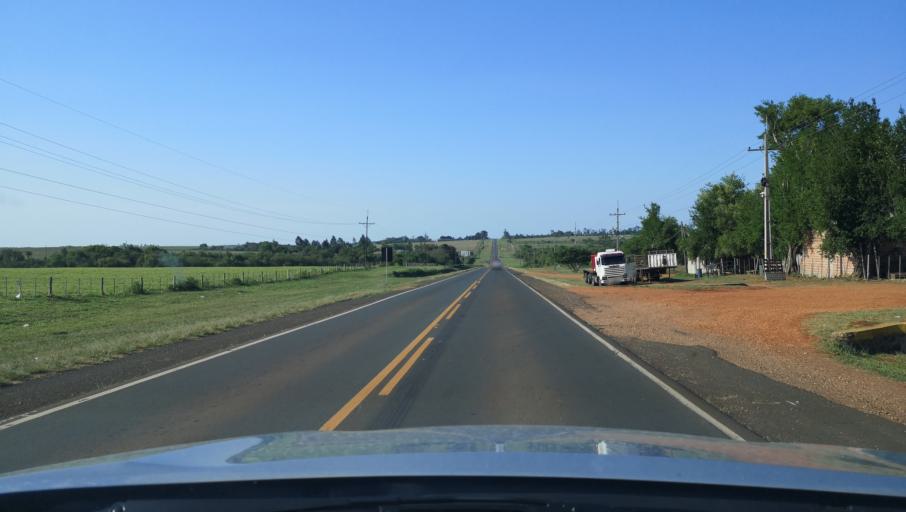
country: PY
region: Misiones
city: Santa Maria
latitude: -26.8373
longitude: -57.0344
